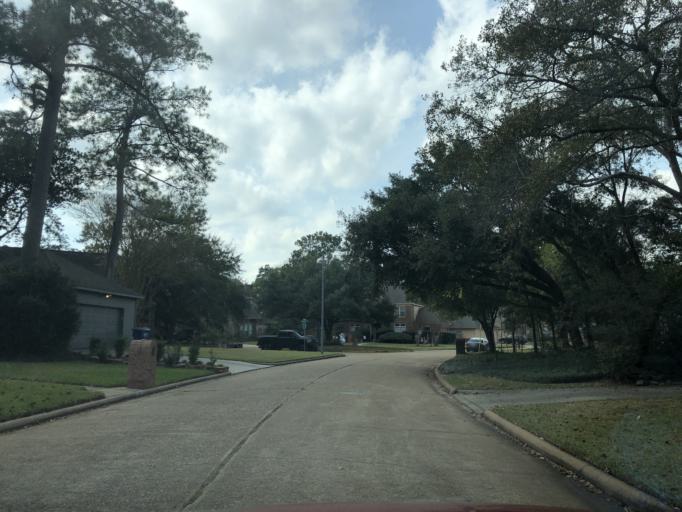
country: US
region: Texas
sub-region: Harris County
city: Tomball
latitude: 30.0309
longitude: -95.5372
